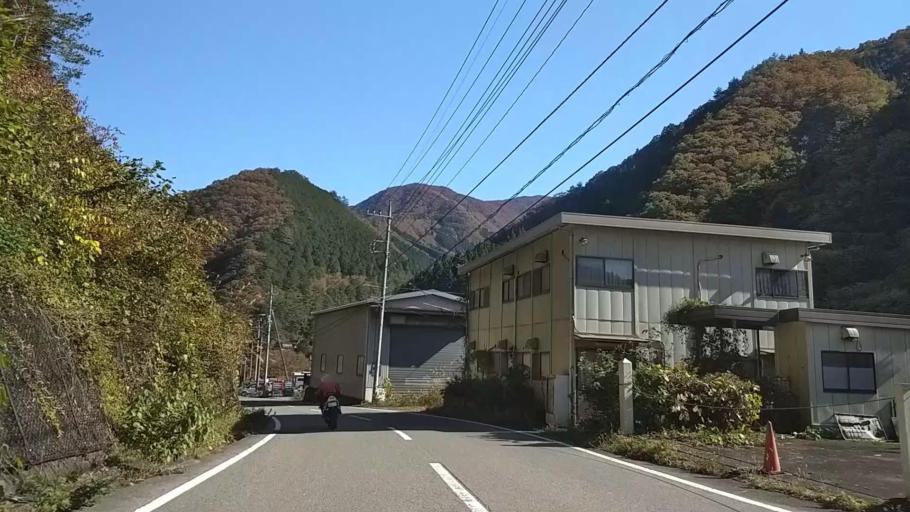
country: JP
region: Yamanashi
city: Otsuki
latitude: 35.7605
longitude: 138.9753
